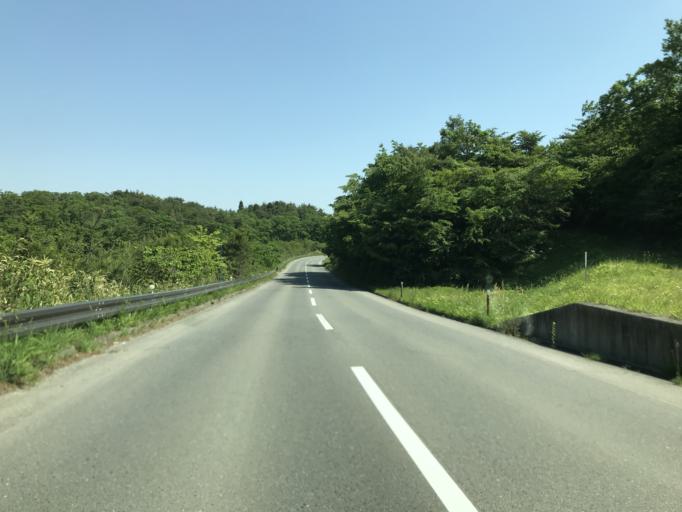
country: JP
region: Miyagi
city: Marumori
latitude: 37.8195
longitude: 140.8799
